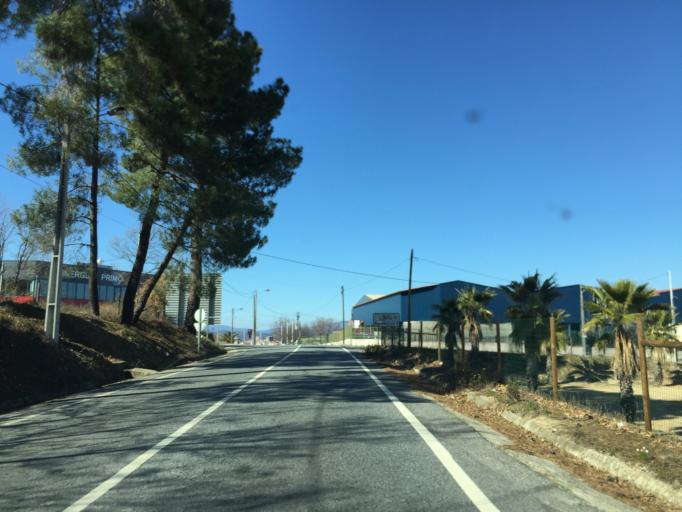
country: PT
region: Castelo Branco
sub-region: Concelho do Fundao
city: Fundao
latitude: 40.1311
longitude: -7.4849
